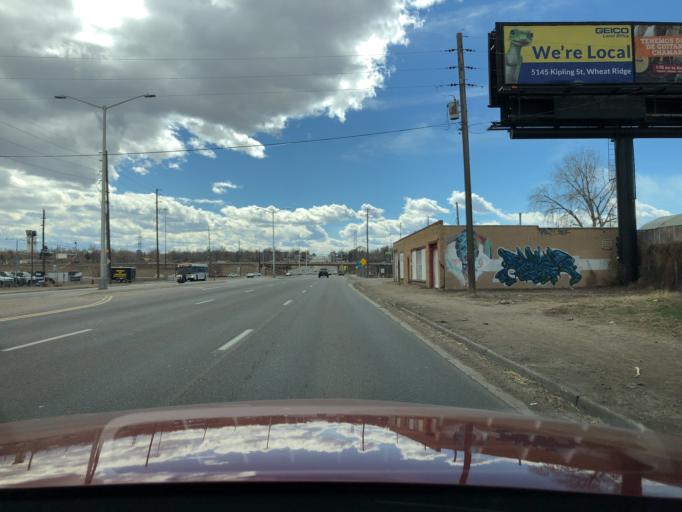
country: US
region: Colorado
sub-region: Adams County
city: Berkley
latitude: 39.8041
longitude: -105.0254
